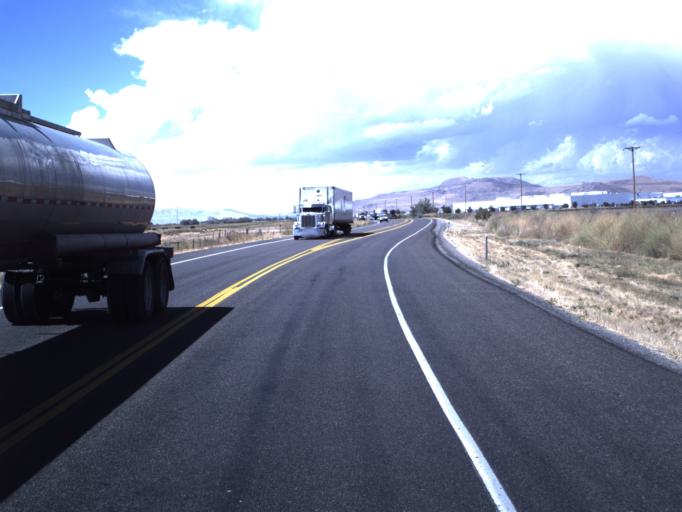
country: US
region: Utah
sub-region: Box Elder County
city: Honeyville
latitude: 41.5558
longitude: -112.1330
